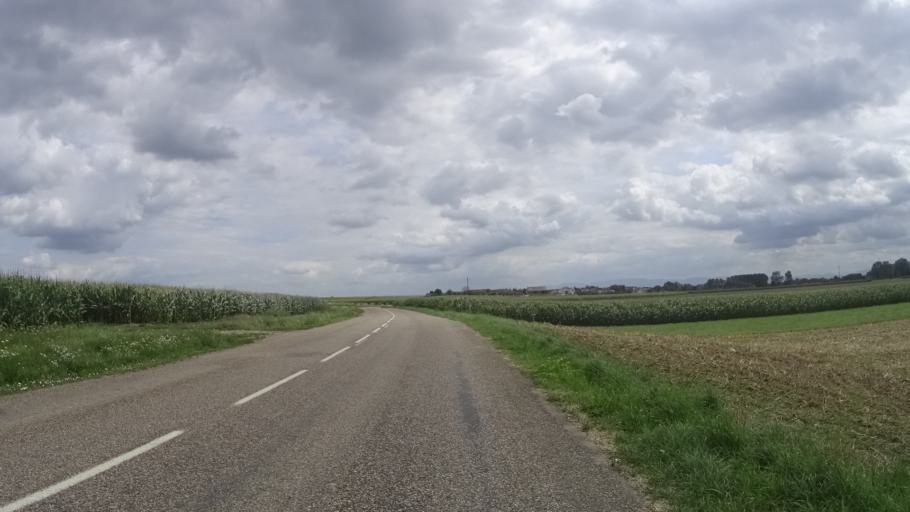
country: FR
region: Alsace
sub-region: Departement du Bas-Rhin
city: Geudertheim
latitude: 48.7211
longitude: 7.7692
